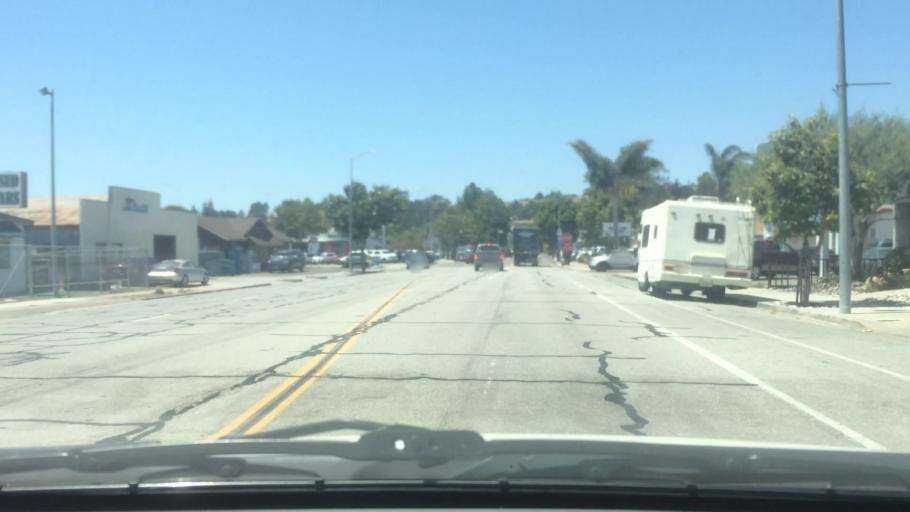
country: US
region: California
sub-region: San Luis Obispo County
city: Arroyo Grande
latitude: 35.1190
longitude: -120.5758
